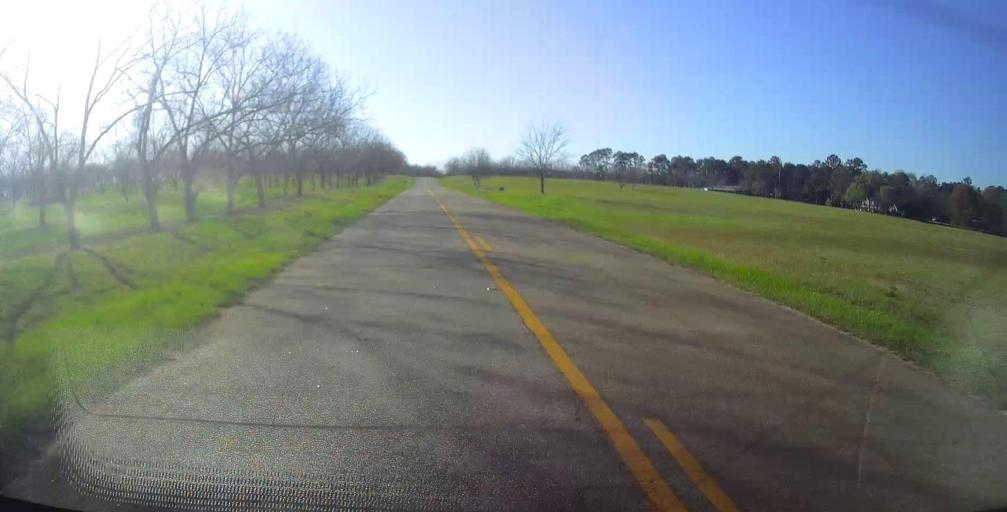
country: US
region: Georgia
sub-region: Houston County
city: Perry
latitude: 32.3648
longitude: -83.6730
